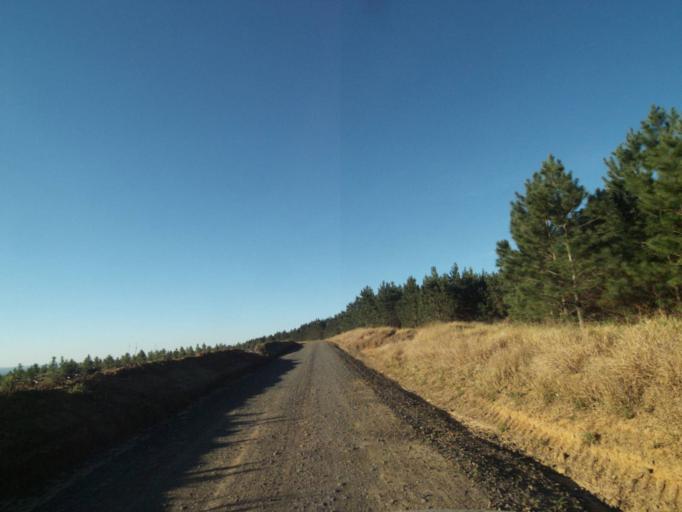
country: BR
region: Parana
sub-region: Telemaco Borba
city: Telemaco Borba
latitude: -24.4545
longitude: -50.6012
